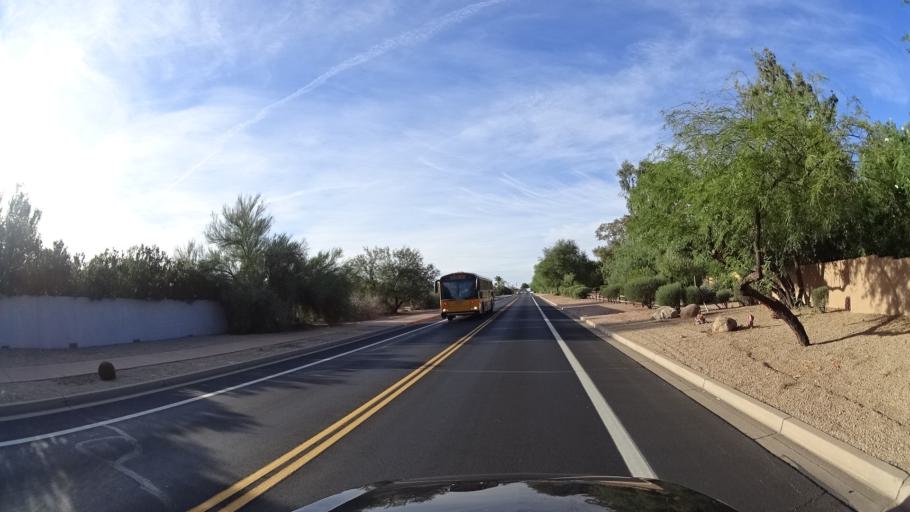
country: US
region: Arizona
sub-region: Maricopa County
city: Paradise Valley
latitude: 33.5277
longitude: -111.9432
